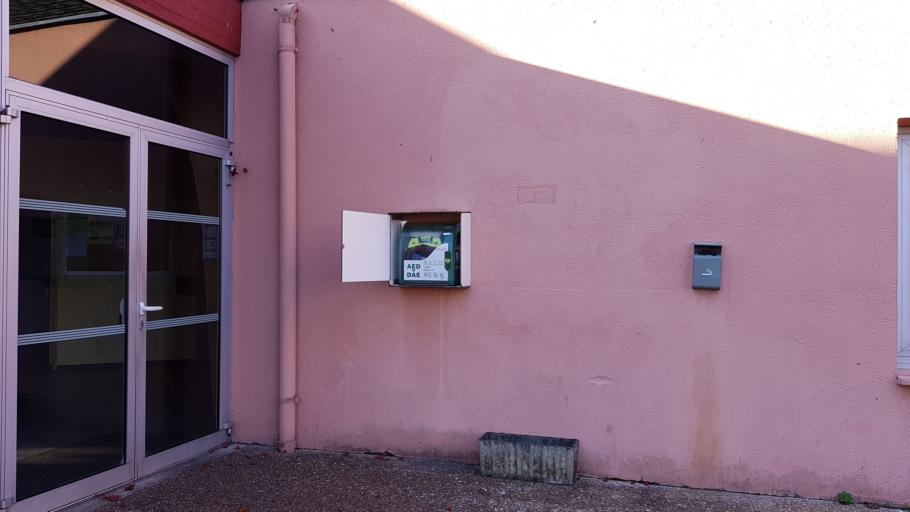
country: FR
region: Aquitaine
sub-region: Departement des Landes
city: Saint-Paul-les-Dax
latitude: 43.7259
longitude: -1.0809
